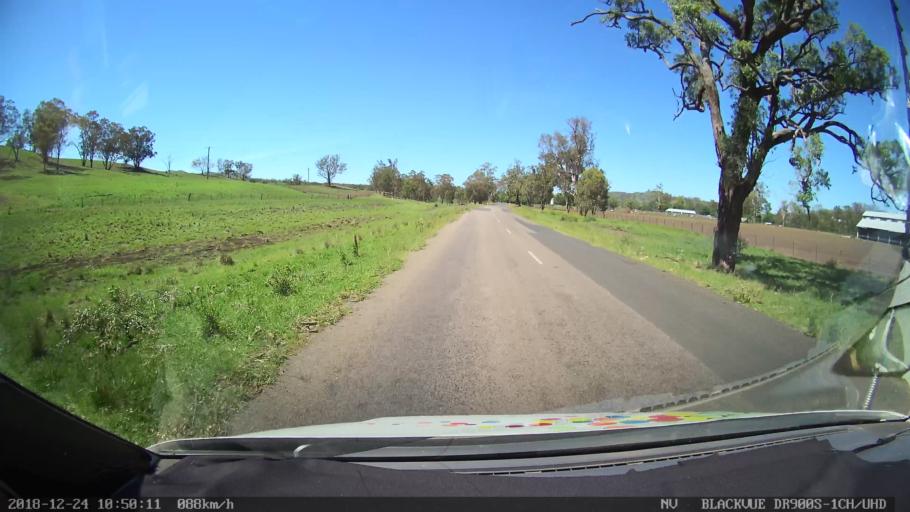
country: AU
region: New South Wales
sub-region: Upper Hunter Shire
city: Merriwa
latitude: -31.9571
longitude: 150.4245
